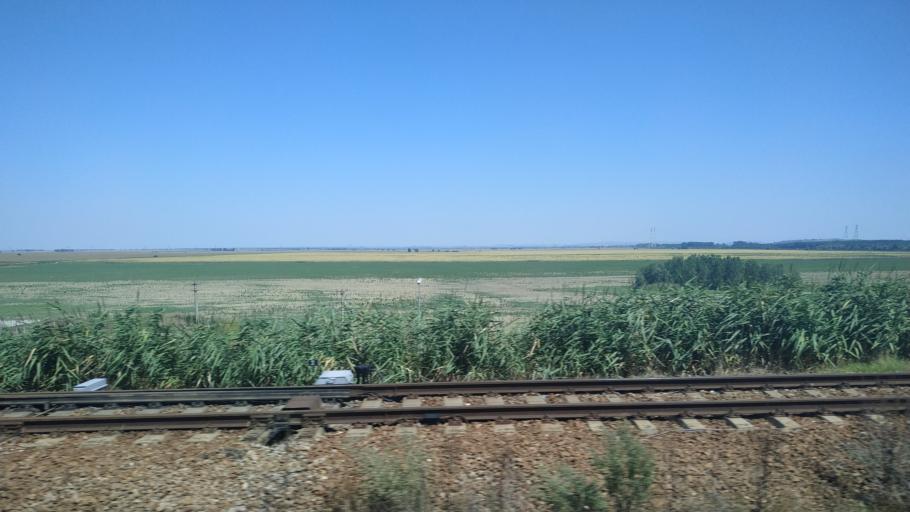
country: RO
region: Constanta
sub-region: Oras Cernavoda
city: Cernavoda
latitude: 44.3464
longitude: 27.9923
